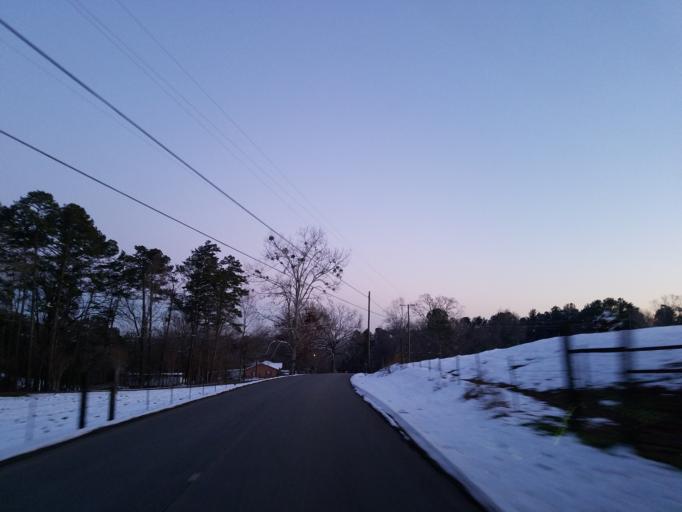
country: US
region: Georgia
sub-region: Pickens County
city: Nelson
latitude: 34.3609
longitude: -84.3689
